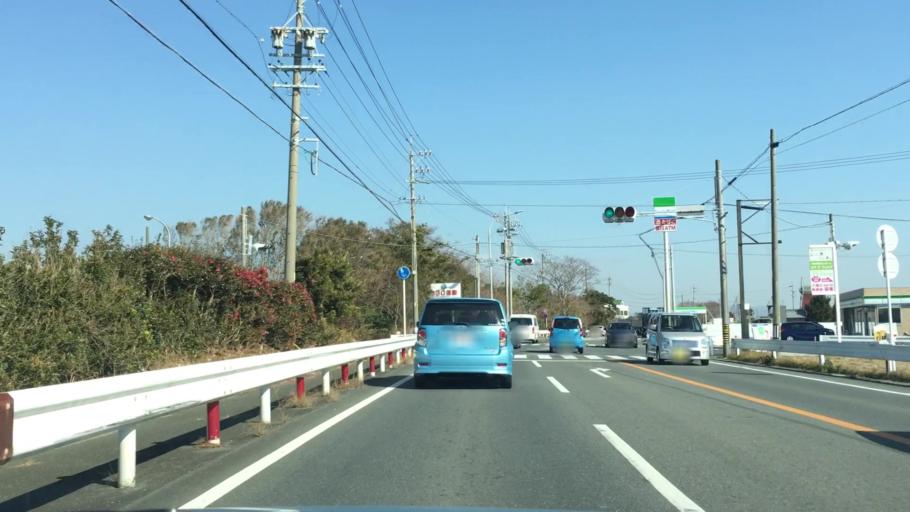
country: JP
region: Aichi
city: Tahara
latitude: 34.6801
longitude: 137.3129
